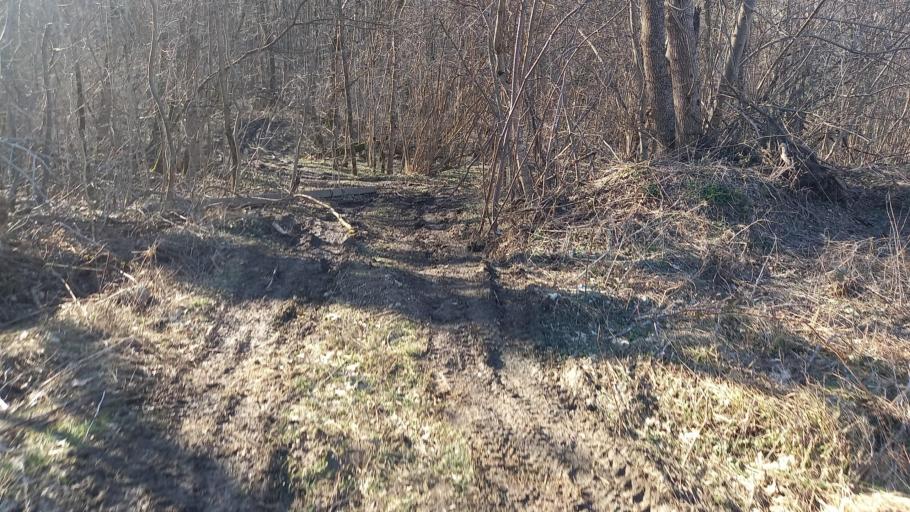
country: RU
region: Krasnodarskiy
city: Goryachiy Klyuch
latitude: 44.6897
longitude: 38.9777
